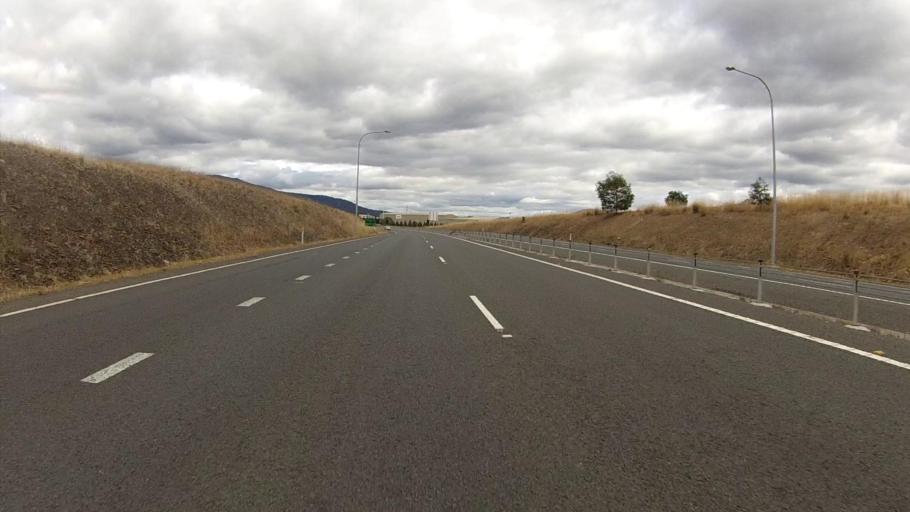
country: AU
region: Tasmania
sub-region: Brighton
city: Bridgewater
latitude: -42.7159
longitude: 147.2419
